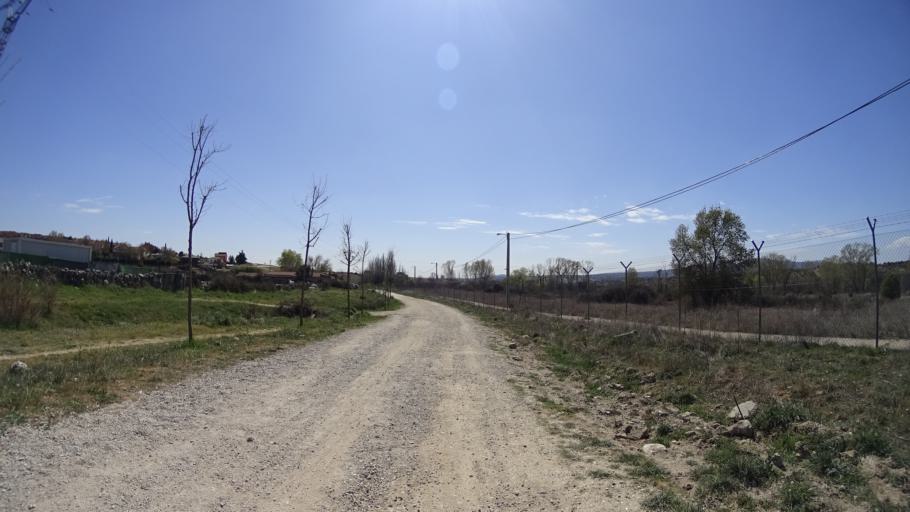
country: ES
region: Madrid
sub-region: Provincia de Madrid
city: Colmenar Viejo
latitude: 40.6737
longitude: -3.7855
